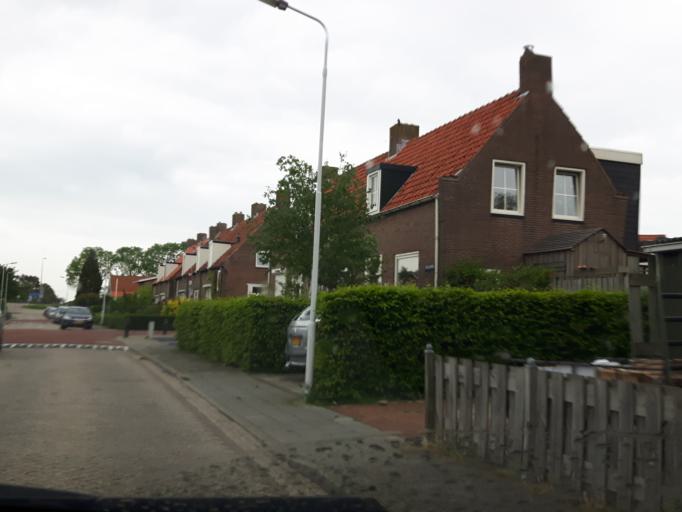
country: NL
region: Zeeland
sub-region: Gemeente Goes
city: Goes
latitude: 51.5017
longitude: 3.8586
